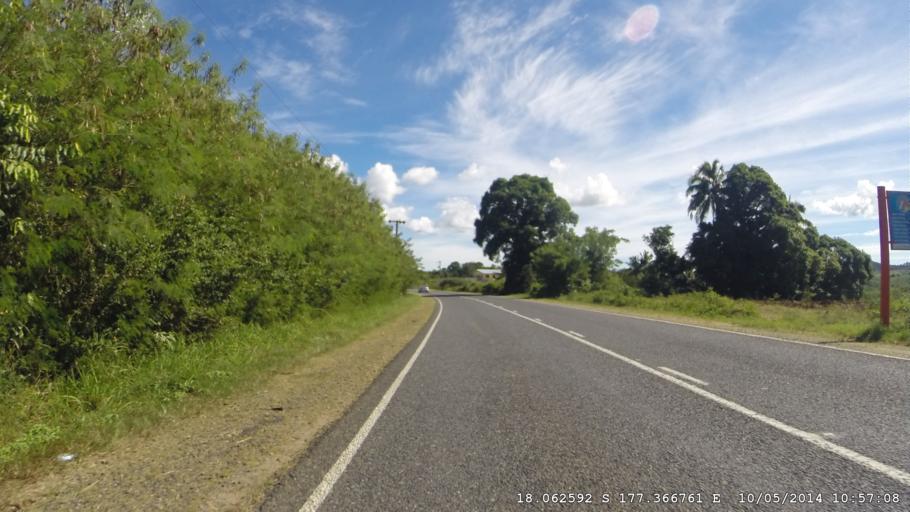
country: FJ
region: Western
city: Nadi
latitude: -18.0626
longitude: 177.3668
